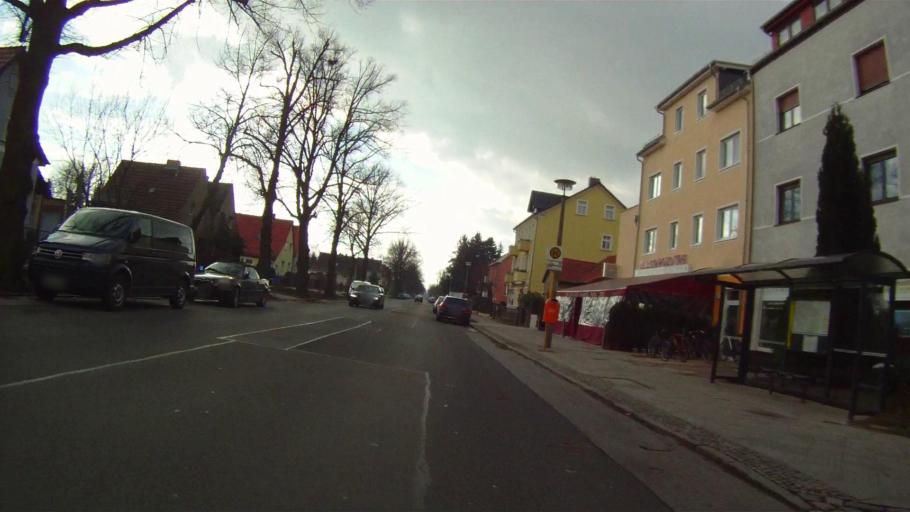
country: DE
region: Berlin
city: Biesdorf
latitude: 52.5195
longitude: 13.5557
